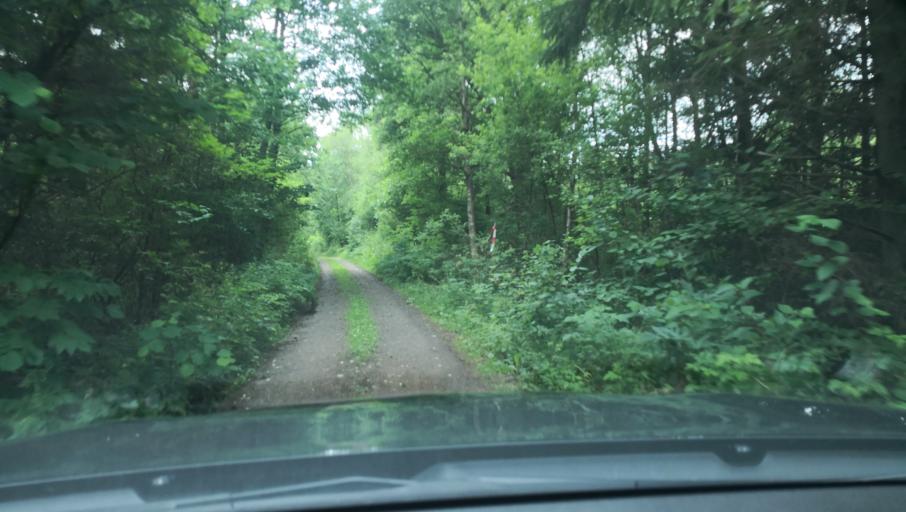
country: SE
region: Skane
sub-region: Simrishamns Kommun
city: Kivik
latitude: 55.6297
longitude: 14.1288
